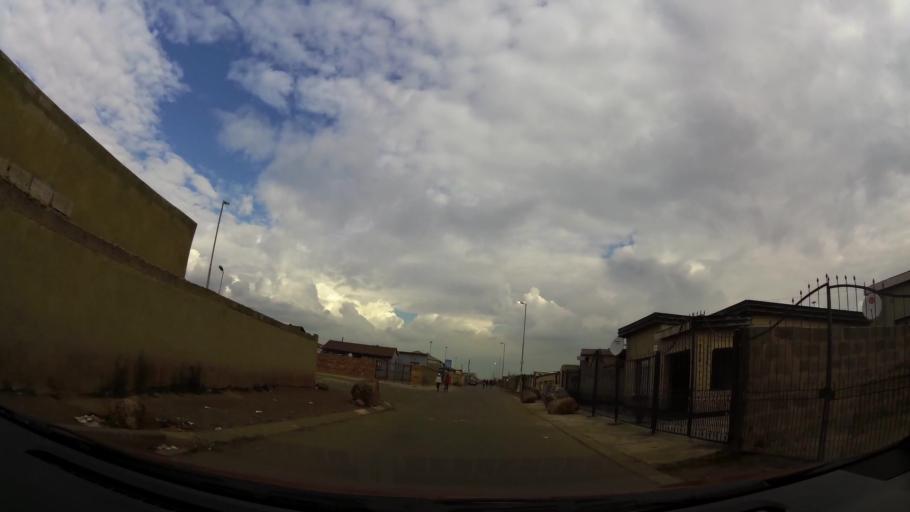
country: ZA
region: Gauteng
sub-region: City of Johannesburg Metropolitan Municipality
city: Soweto
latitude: -26.2454
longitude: 27.8513
